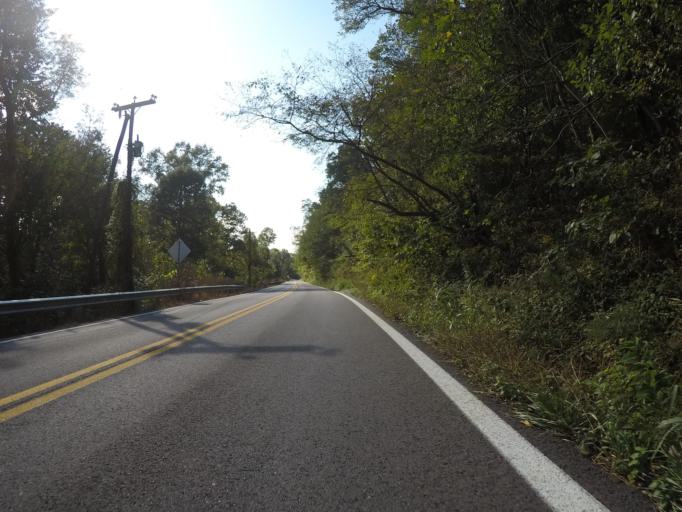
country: US
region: Ohio
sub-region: Lawrence County
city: Burlington
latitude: 38.3728
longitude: -82.5236
